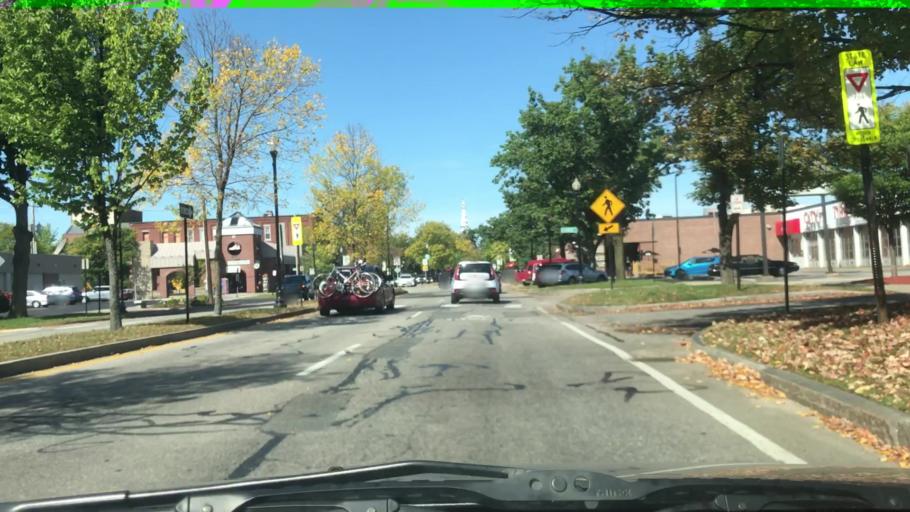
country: US
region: New Hampshire
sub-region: Cheshire County
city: Keene
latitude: 42.9301
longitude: -72.2778
